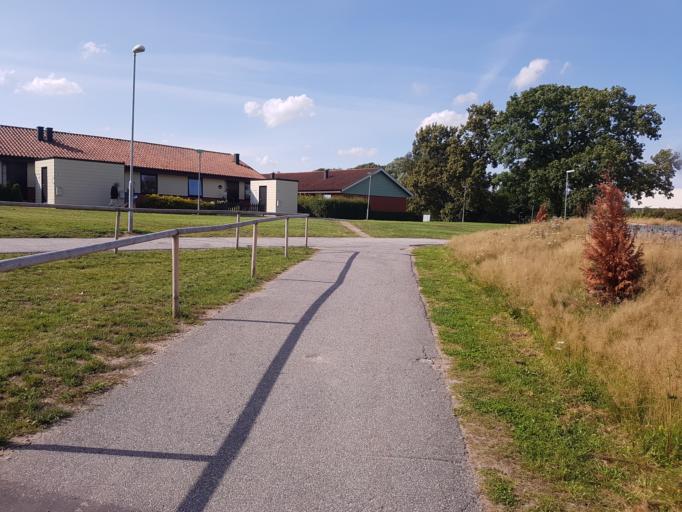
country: SE
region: Skane
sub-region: Sjobo Kommun
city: Sjoebo
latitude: 55.6348
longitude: 13.7001
